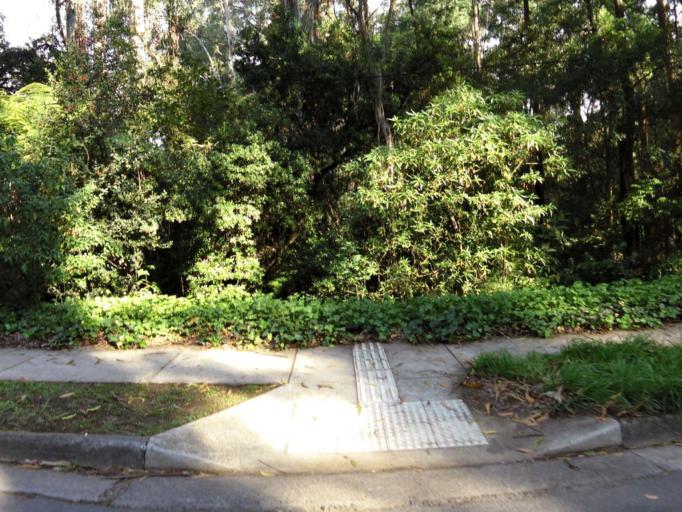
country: AU
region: Victoria
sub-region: Yarra Ranges
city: Monbulk
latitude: -37.8764
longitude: 145.4033
